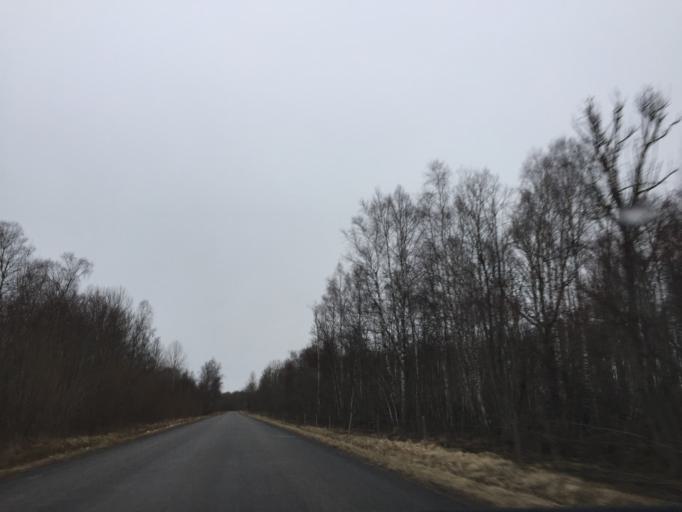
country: EE
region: Laeaene
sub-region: Lihula vald
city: Lihula
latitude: 58.6295
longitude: 23.6328
